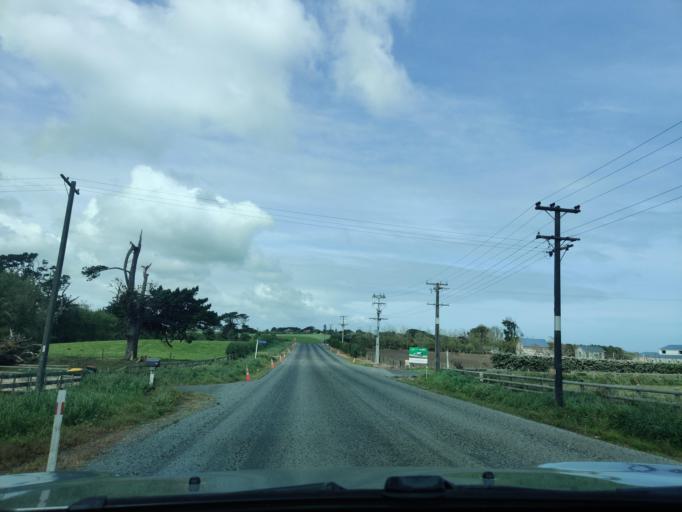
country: NZ
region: Taranaki
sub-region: South Taranaki District
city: Hawera
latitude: -39.5852
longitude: 174.2455
